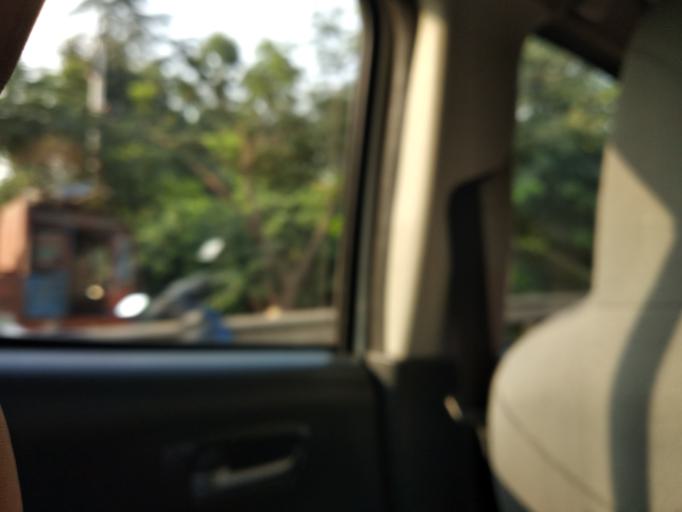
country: IN
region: Andhra Pradesh
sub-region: Vishakhapatnam
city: Visakhapatnam
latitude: 17.6848
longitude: 83.1567
